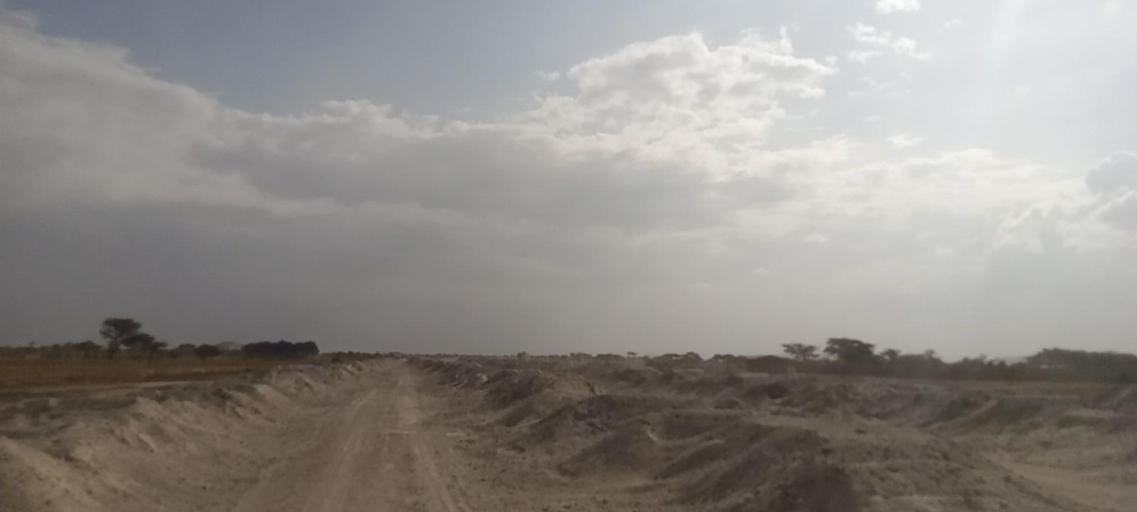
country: ET
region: Oromiya
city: Ziway
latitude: 7.8773
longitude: 38.6731
